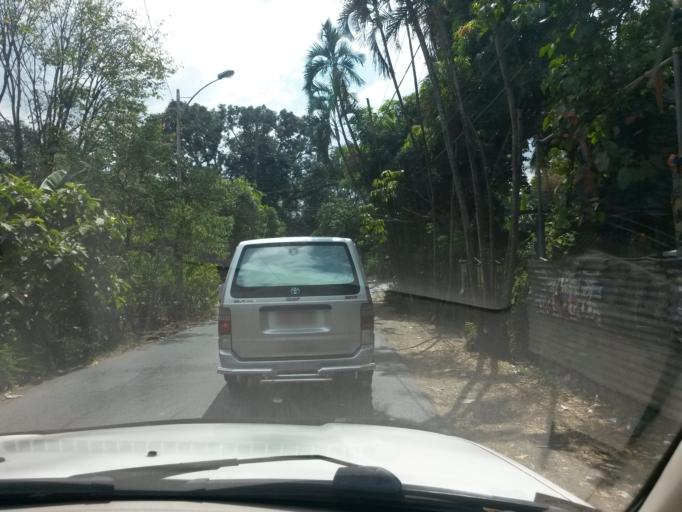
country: PH
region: Metro Manila
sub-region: Quezon City
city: Quezon City
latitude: 14.6524
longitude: 121.0790
